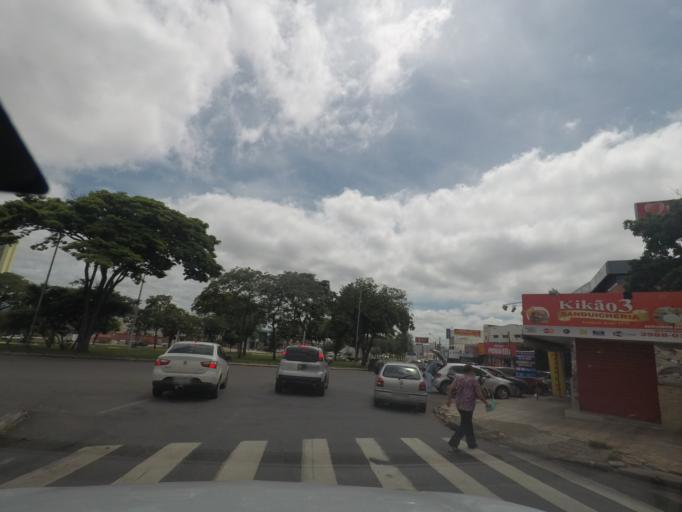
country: BR
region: Goias
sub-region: Goiania
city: Goiania
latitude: -16.6722
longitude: -49.2346
